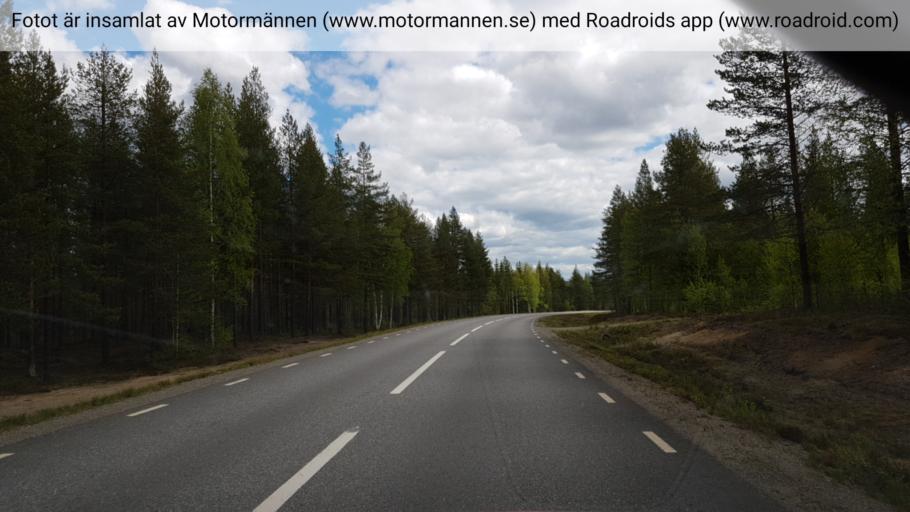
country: SE
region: Vaesterbotten
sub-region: Skelleftea Kommun
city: Langsele
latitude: 64.8190
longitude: 19.9750
